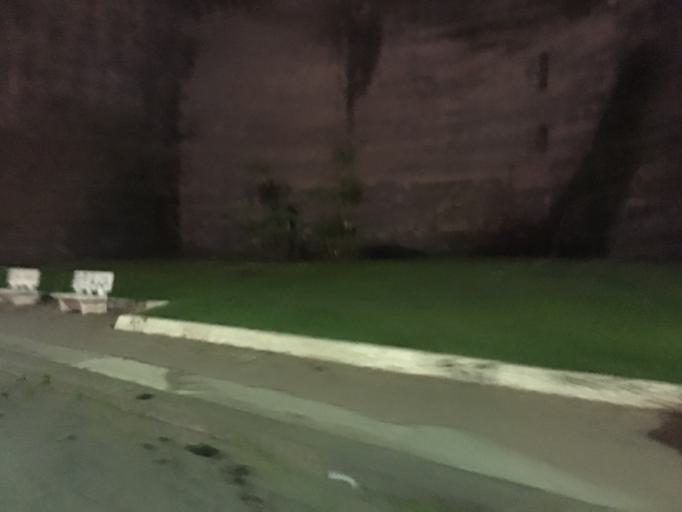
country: IT
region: Campania
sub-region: Provincia di Napoli
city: Napoli
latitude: 40.8384
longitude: 14.2543
